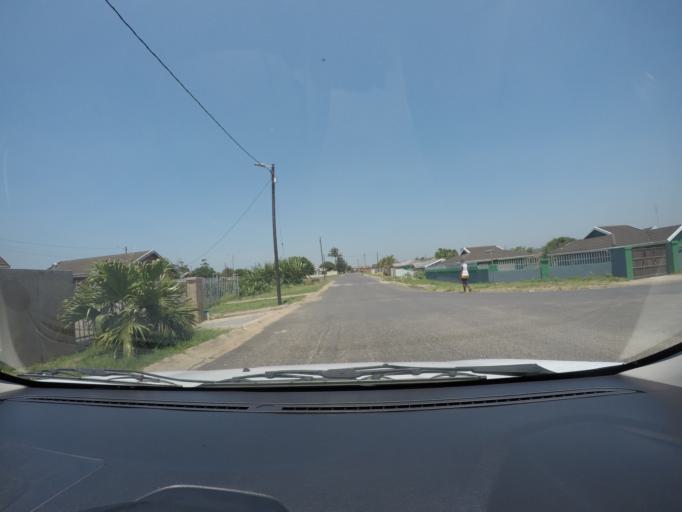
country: ZA
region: KwaZulu-Natal
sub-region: uThungulu District Municipality
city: eSikhawini
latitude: -28.8717
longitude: 31.9210
